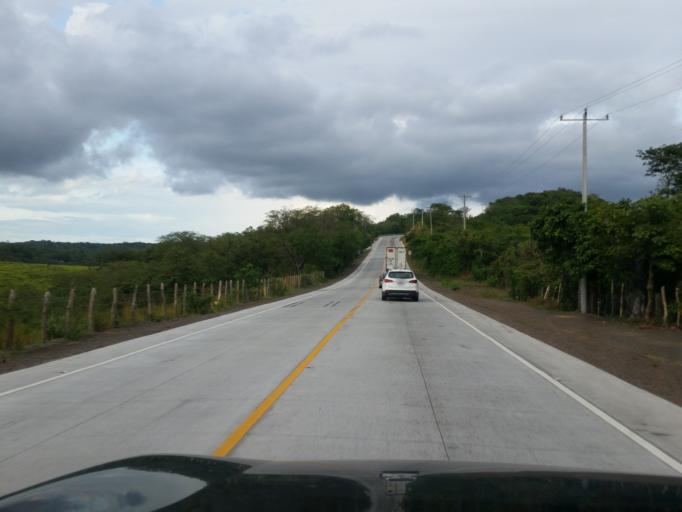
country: NI
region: Managua
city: Ciudad Sandino
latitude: 12.0803
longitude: -86.4203
